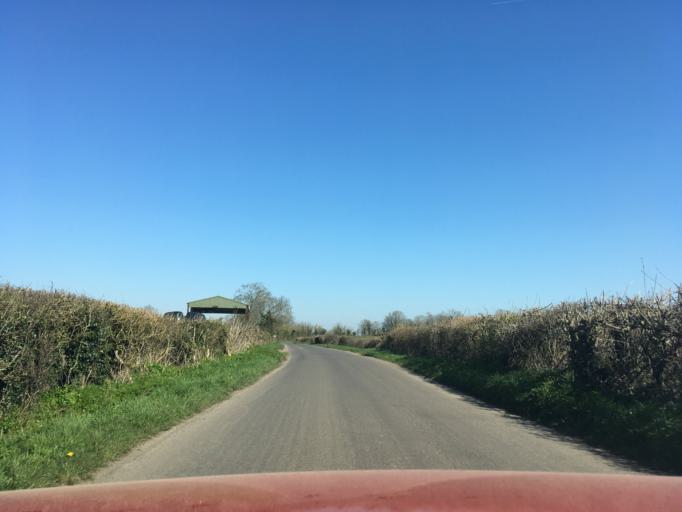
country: GB
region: England
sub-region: South Gloucestershire
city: Hill
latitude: 51.6680
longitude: -2.5044
